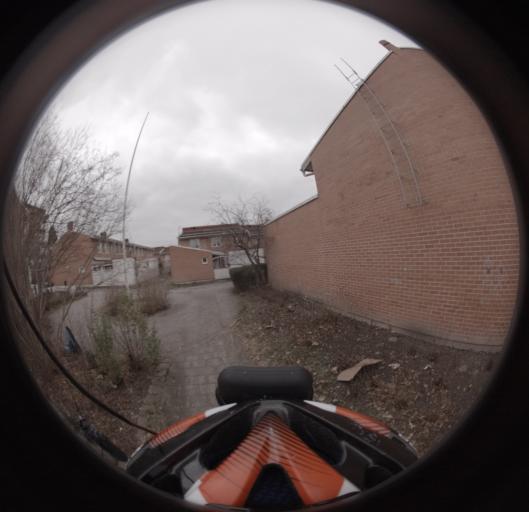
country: SE
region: Stockholm
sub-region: Upplands Vasby Kommun
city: Upplands Vaesby
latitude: 59.4833
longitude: 17.9288
